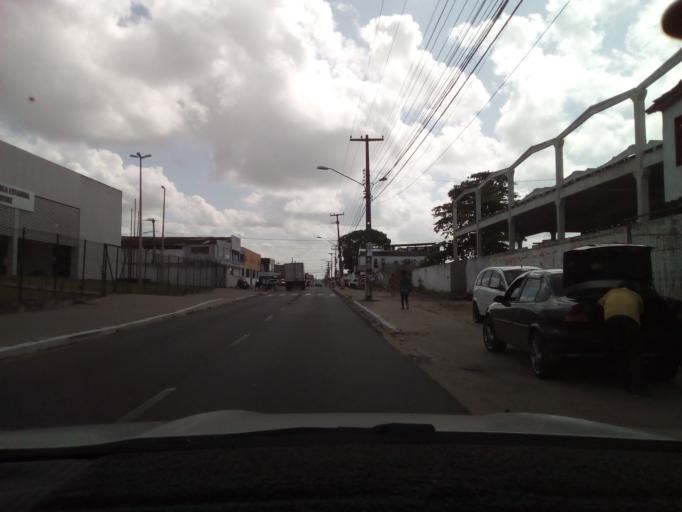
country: BR
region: Paraiba
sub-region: Bayeux
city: Bayeux
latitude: -7.1237
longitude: -34.9200
